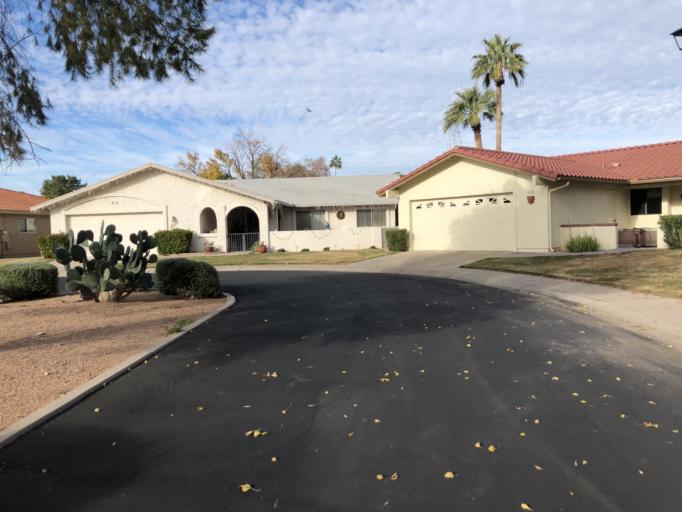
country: US
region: Arizona
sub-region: Maricopa County
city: Gilbert
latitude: 33.4036
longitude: -111.6904
